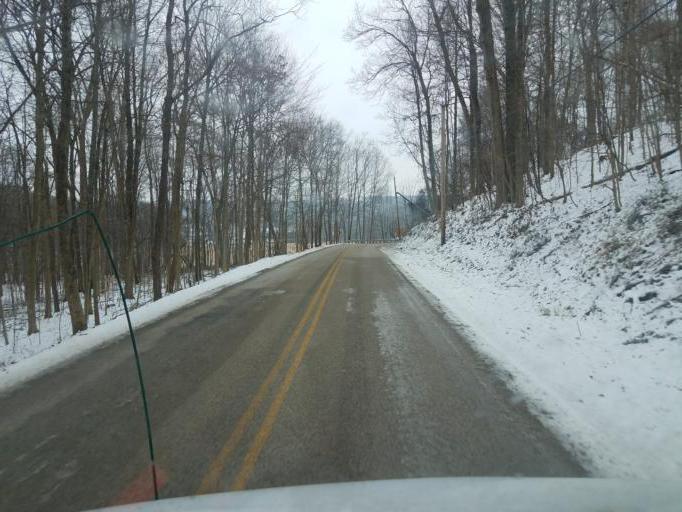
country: US
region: Ohio
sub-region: Sandusky County
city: Bellville
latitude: 40.6649
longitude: -82.4151
